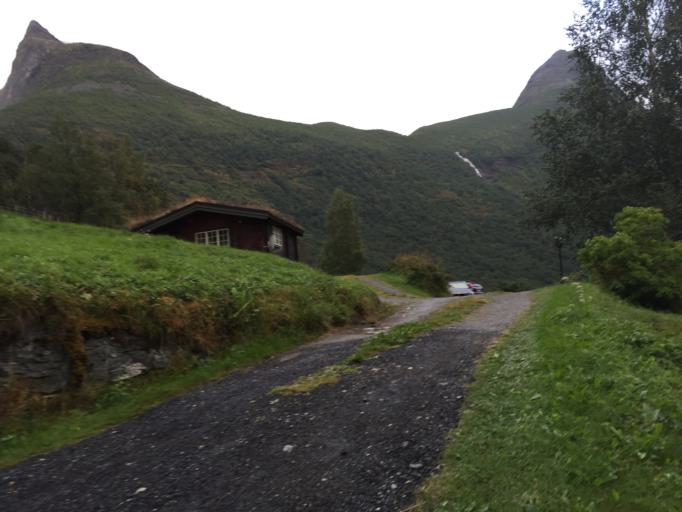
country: NO
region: More og Romsdal
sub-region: Norddal
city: Valldal
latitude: 62.1009
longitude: 7.2177
